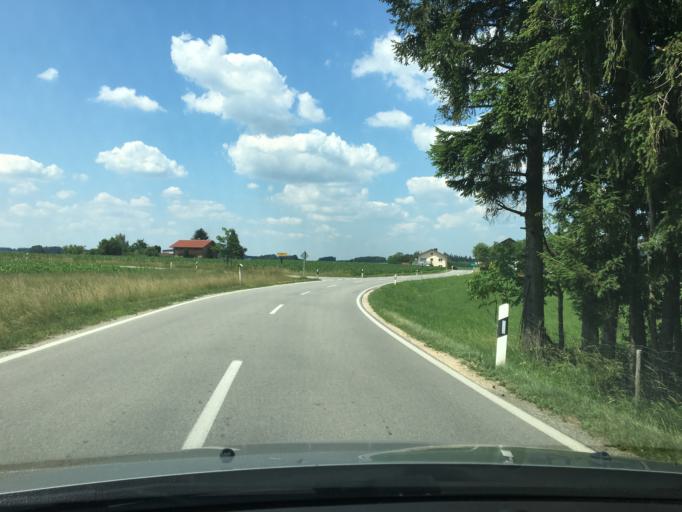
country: DE
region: Bavaria
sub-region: Upper Bavaria
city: Neumarkt-Sankt Veit
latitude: 48.3755
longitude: 12.5068
